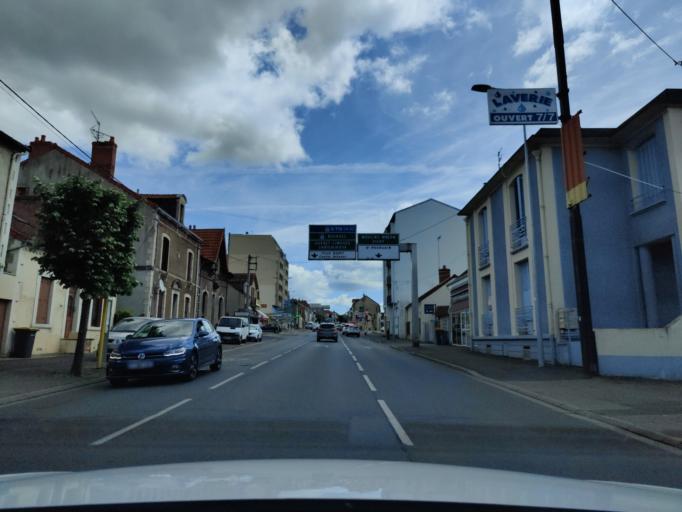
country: FR
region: Auvergne
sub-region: Departement de l'Allier
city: Desertines
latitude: 46.3439
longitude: 2.6126
